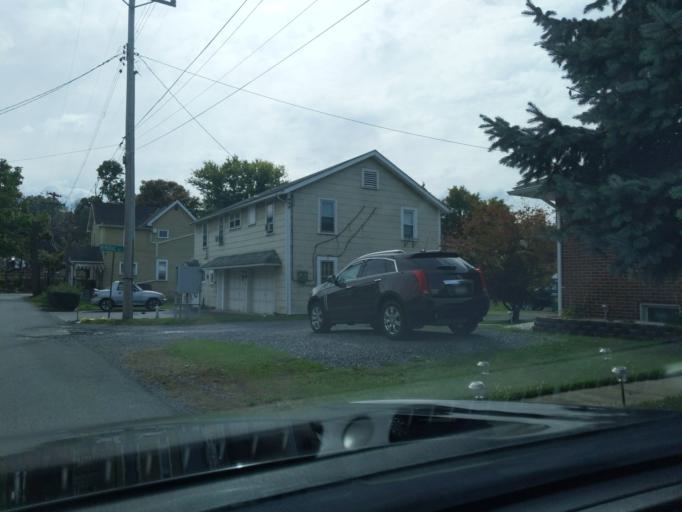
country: US
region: Pennsylvania
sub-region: Blair County
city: Hollidaysburg
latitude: 40.4289
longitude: -78.4029
